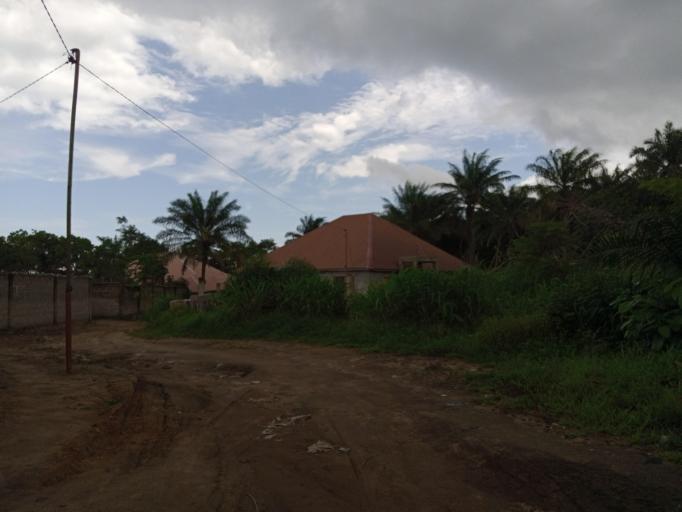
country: SL
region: Northern Province
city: Masoyila
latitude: 8.5788
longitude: -13.1656
